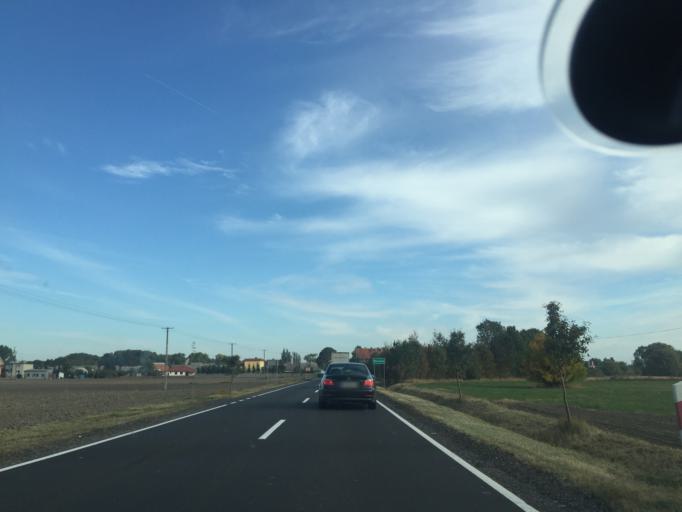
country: PL
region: Kujawsko-Pomorskie
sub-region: Powiat mogilenski
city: Mogilno
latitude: 52.6109
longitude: 17.9303
